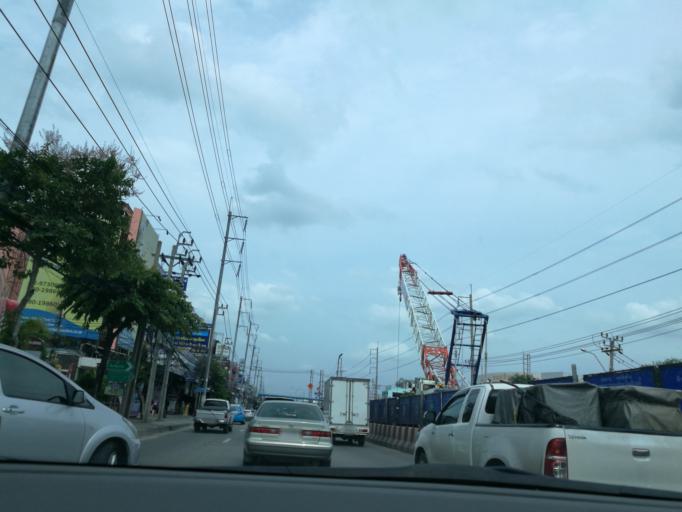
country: TH
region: Bangkok
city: Bang Khen
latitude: 13.8591
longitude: 100.6247
